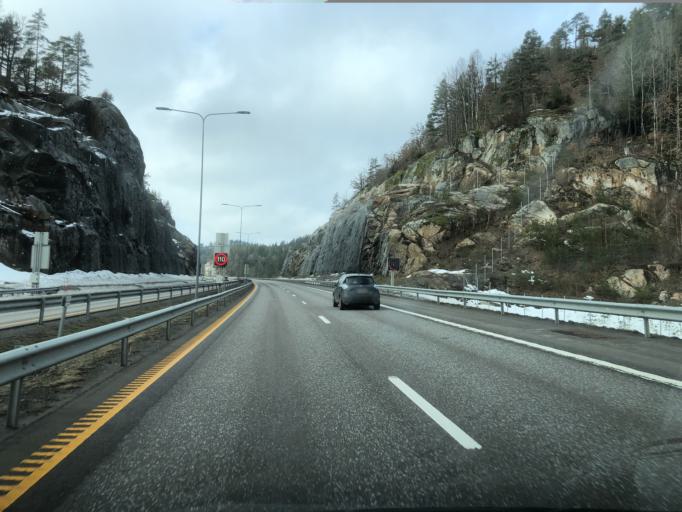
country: NO
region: Vestfold
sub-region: Larvik
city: Larvik
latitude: 59.0769
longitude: 9.8863
